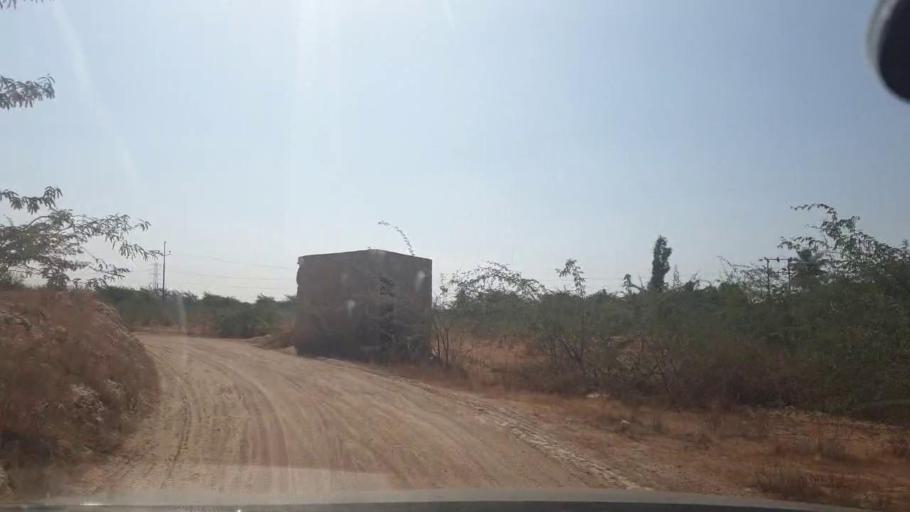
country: PK
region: Sindh
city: Malir Cantonment
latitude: 25.1683
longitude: 67.2030
